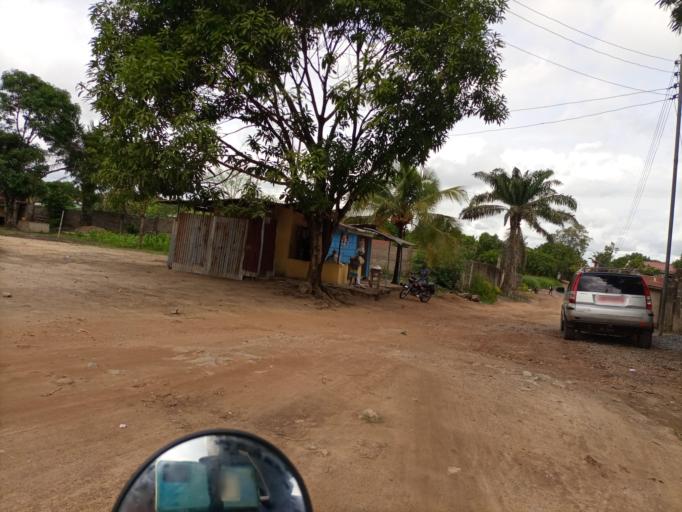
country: SL
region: Southern Province
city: Bo
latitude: 7.9704
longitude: -11.7617
